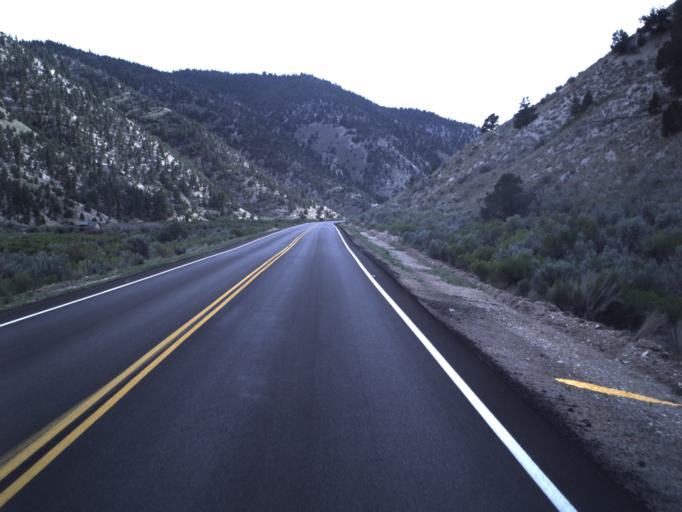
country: US
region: Utah
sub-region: Duchesne County
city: Duchesne
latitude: 40.0189
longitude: -110.5600
